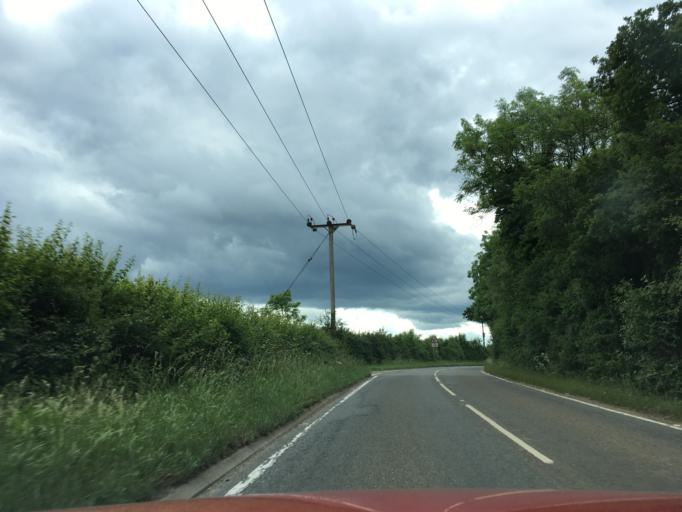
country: GB
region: England
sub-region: Central Bedfordshire
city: Potsgrove
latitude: 51.9557
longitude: -0.6450
